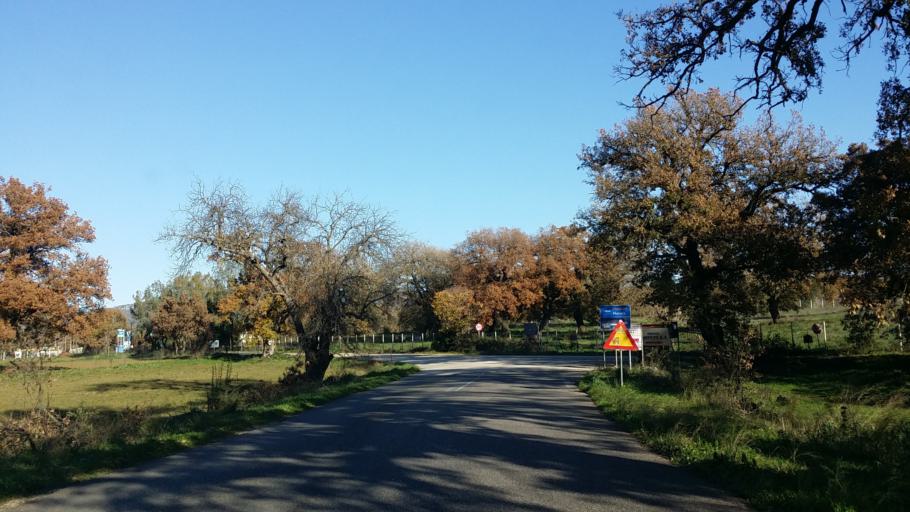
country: GR
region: West Greece
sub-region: Nomos Aitolias kai Akarnanias
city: Fitiai
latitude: 38.6163
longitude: 21.1425
